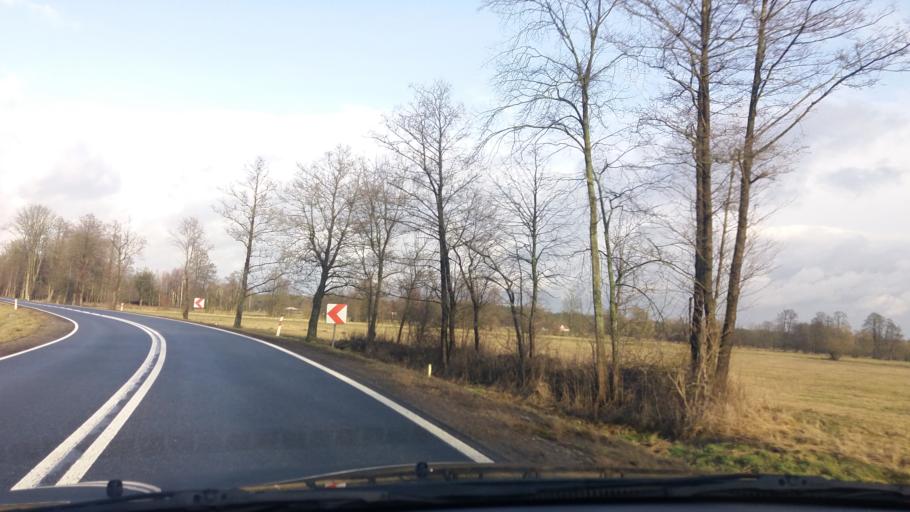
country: PL
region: Masovian Voivodeship
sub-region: Powiat przasnyski
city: Chorzele
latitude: 53.2867
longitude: 20.9088
